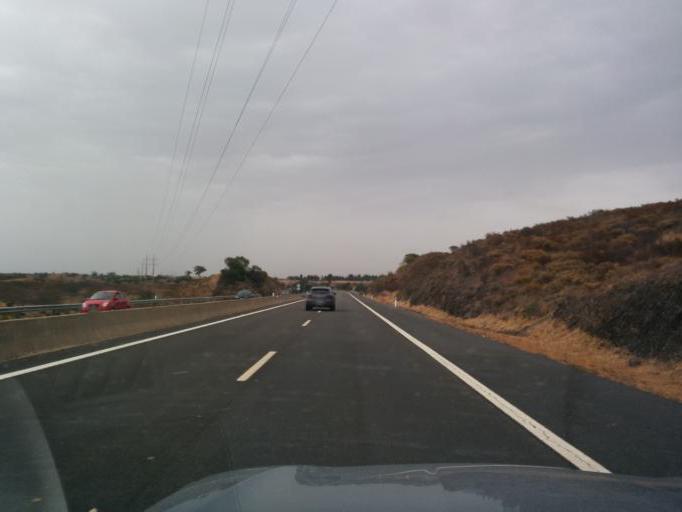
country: PT
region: Faro
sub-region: Tavira
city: Tavira
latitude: 37.1857
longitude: -7.5631
